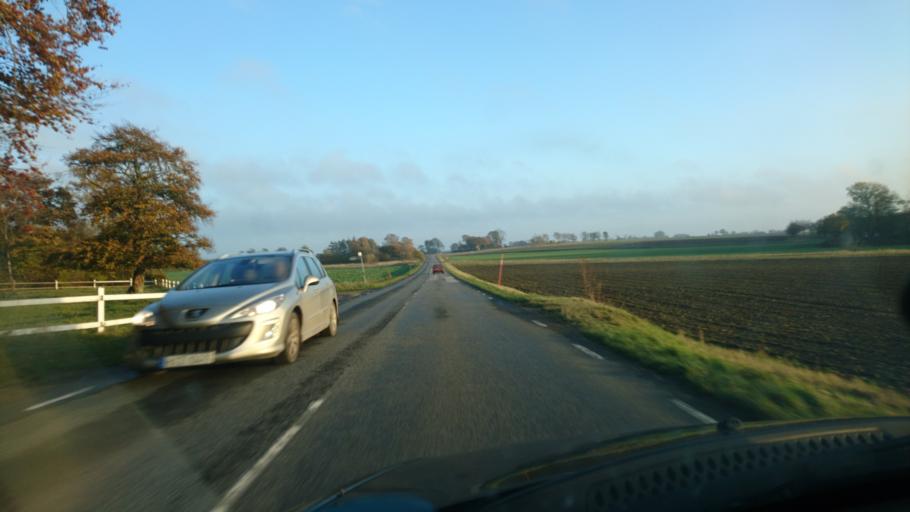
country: SE
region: Skane
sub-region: Tomelilla Kommun
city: Tomelilla
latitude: 55.4624
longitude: 14.1012
